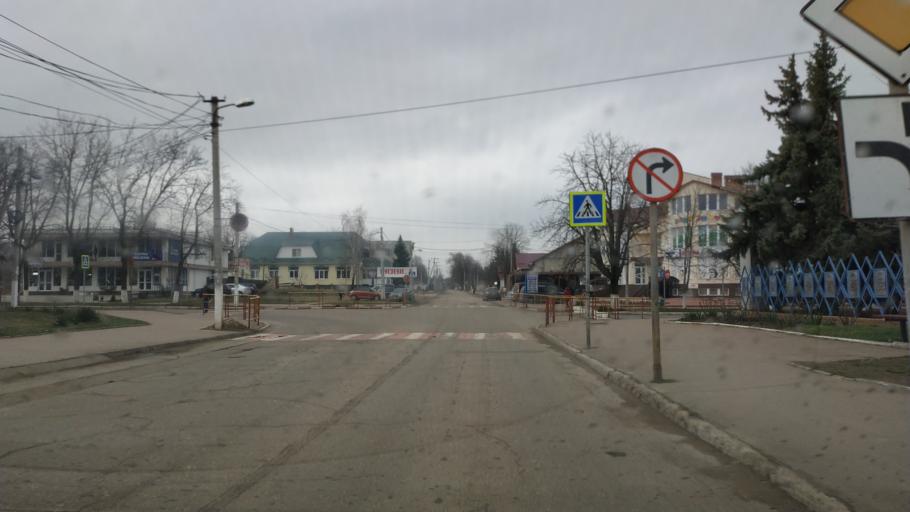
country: MD
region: Leova
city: Leova
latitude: 46.4783
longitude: 28.2538
